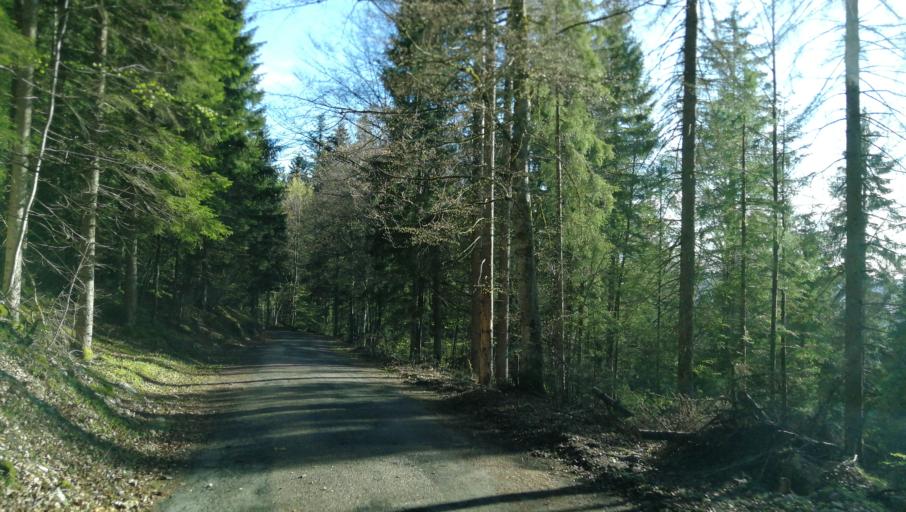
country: FR
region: Rhone-Alpes
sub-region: Departement de l'Ain
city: Chatillon-en-Michaille
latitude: 46.2615
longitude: 5.7978
